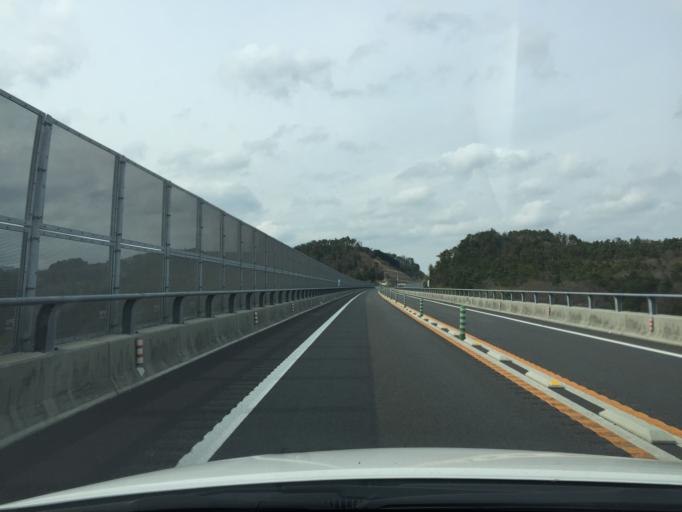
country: JP
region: Fukushima
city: Namie
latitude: 37.4323
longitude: 140.9596
